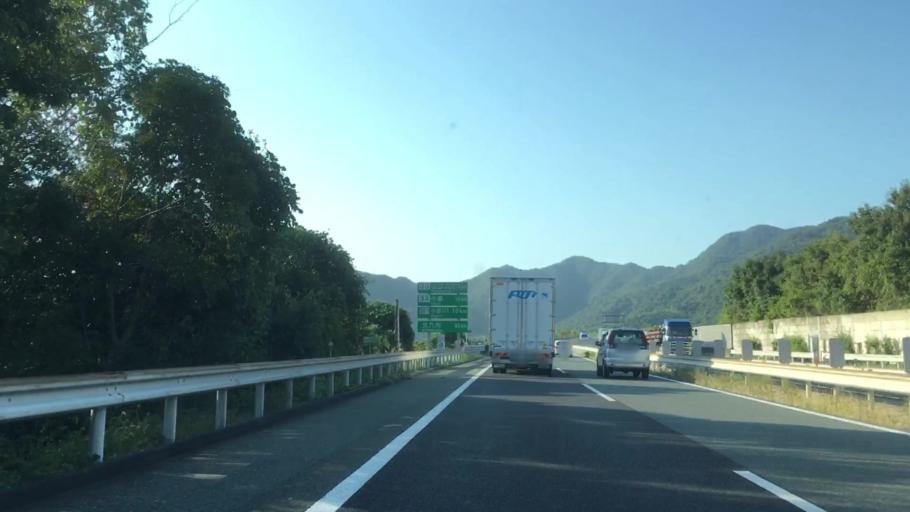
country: JP
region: Yamaguchi
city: Ogori-shimogo
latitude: 34.0916
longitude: 131.4575
